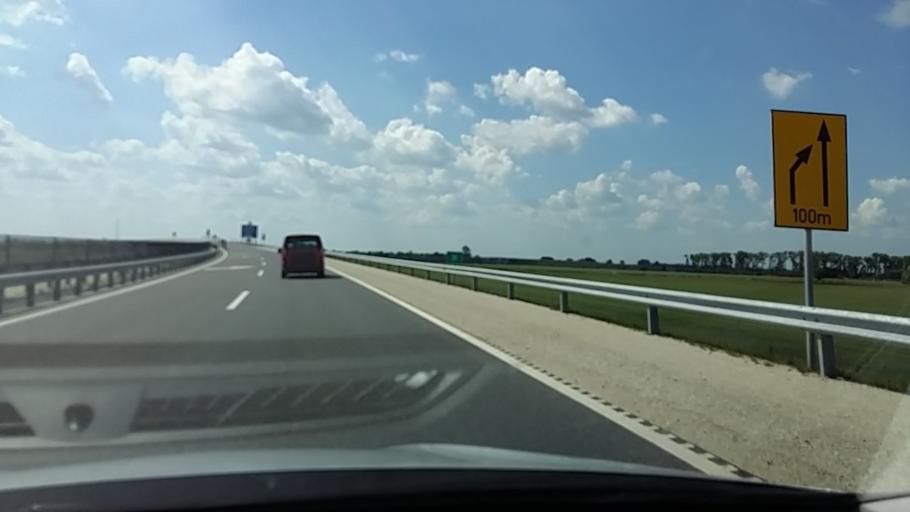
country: HU
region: Gyor-Moson-Sopron
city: Farad
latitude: 47.5902
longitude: 17.1991
